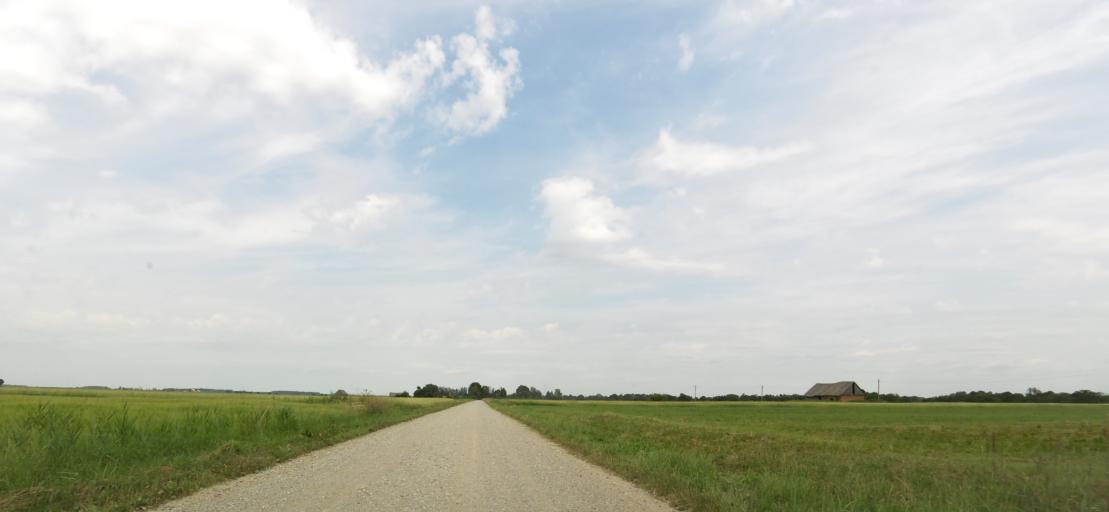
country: LT
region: Panevezys
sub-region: Birzai
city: Birzai
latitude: 56.3518
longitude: 24.7476
